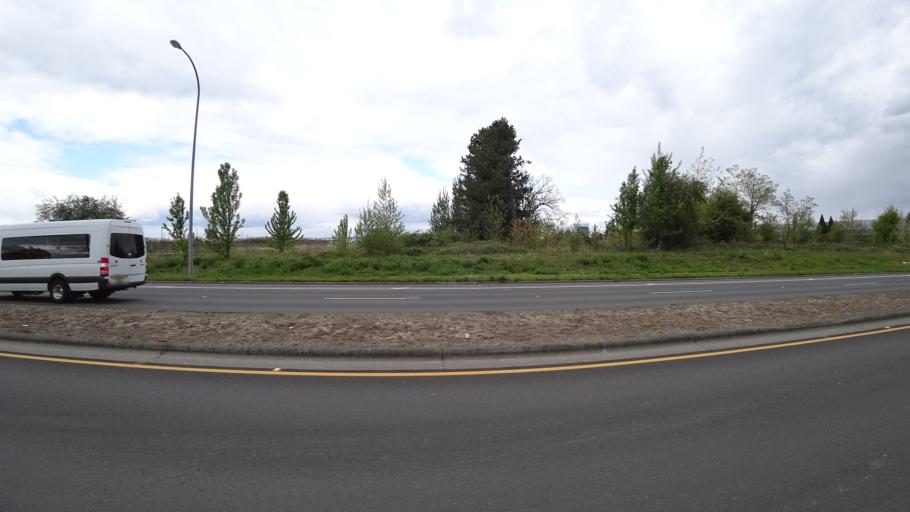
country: US
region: Oregon
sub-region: Washington County
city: Rockcreek
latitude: 45.5509
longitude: -122.9223
